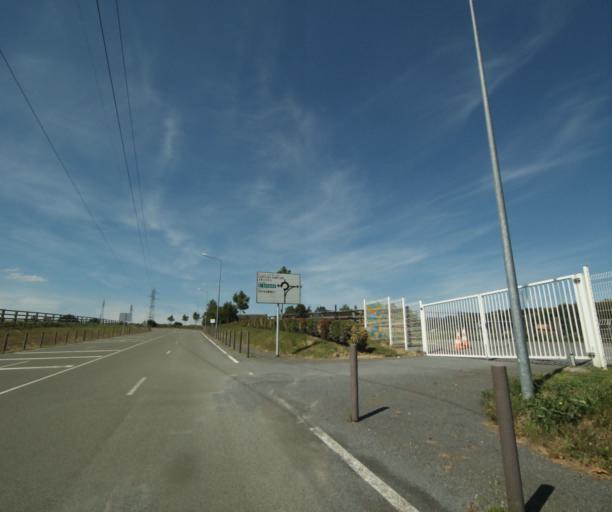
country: FR
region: Pays de la Loire
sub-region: Departement de la Mayenne
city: Montigne-le-Brillant
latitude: 48.0389
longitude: -0.7998
